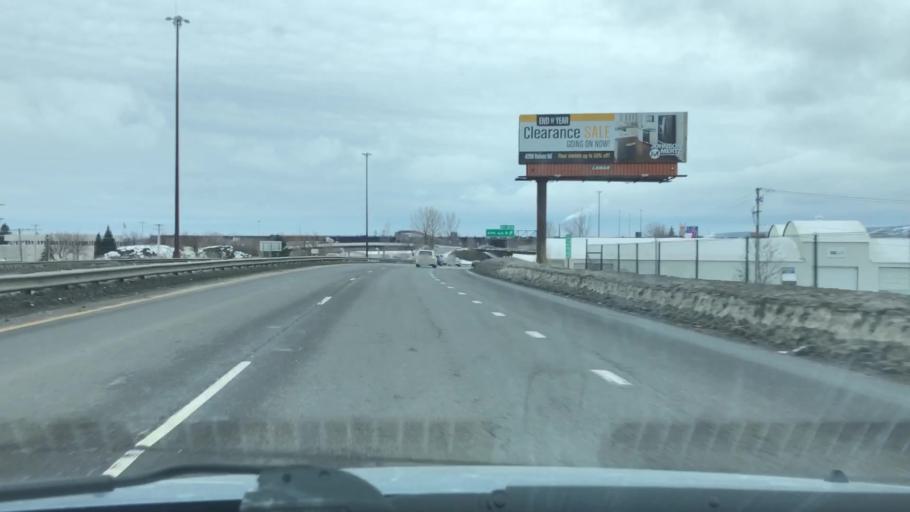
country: US
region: Minnesota
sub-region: Saint Louis County
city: Duluth
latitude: 46.7621
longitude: -92.1261
